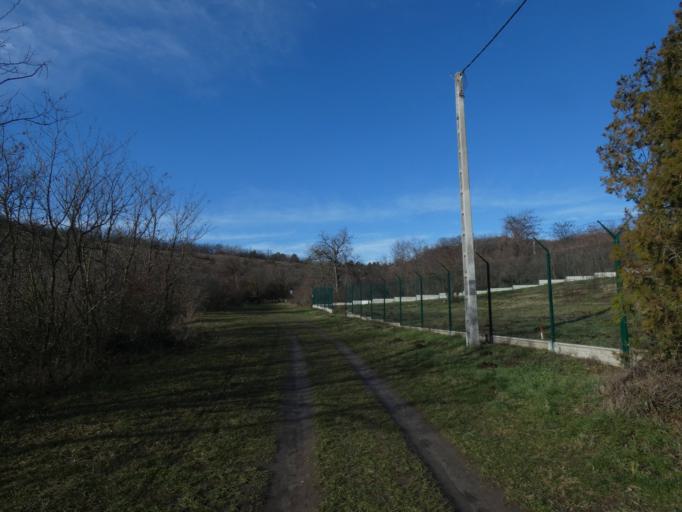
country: HU
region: Pest
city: Erd
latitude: 47.3946
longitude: 18.8779
